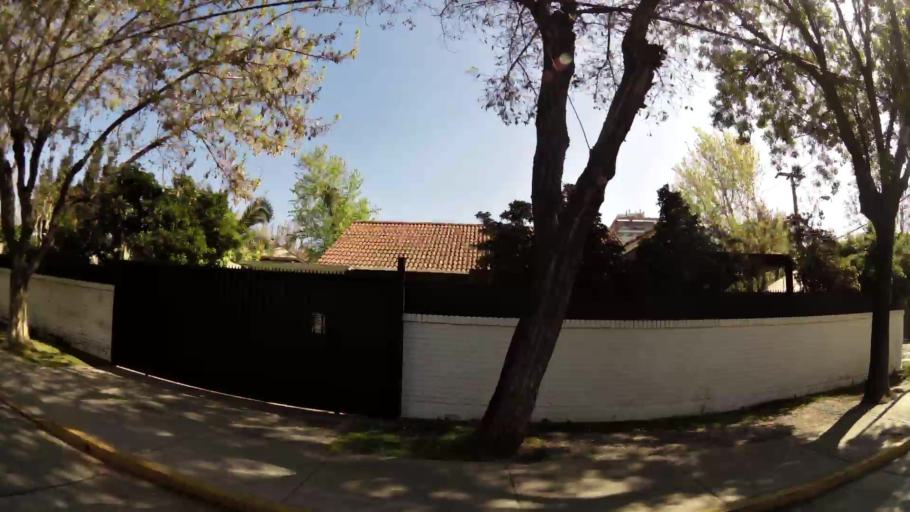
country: CL
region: Santiago Metropolitan
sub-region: Provincia de Santiago
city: Villa Presidente Frei, Nunoa, Santiago, Chile
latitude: -33.4184
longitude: -70.5799
